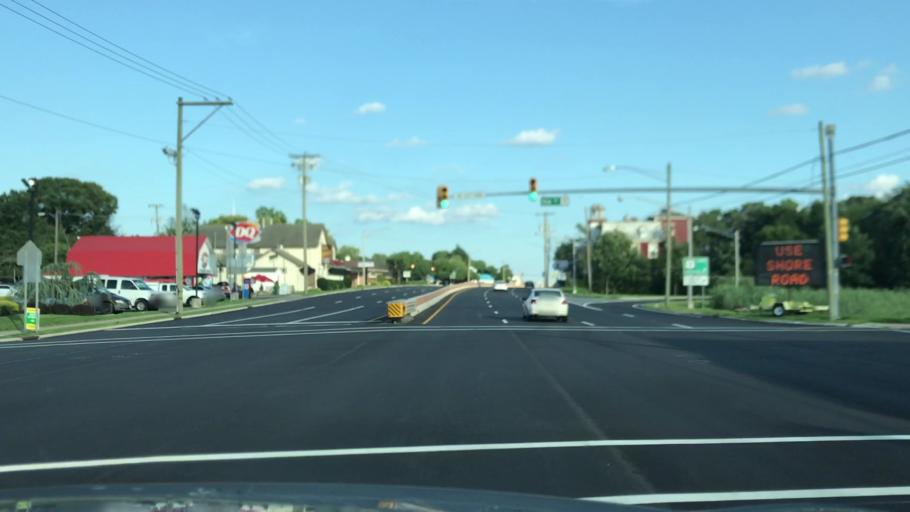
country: US
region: New Jersey
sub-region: Atlantic County
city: Absecon
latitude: 39.4281
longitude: -74.5056
